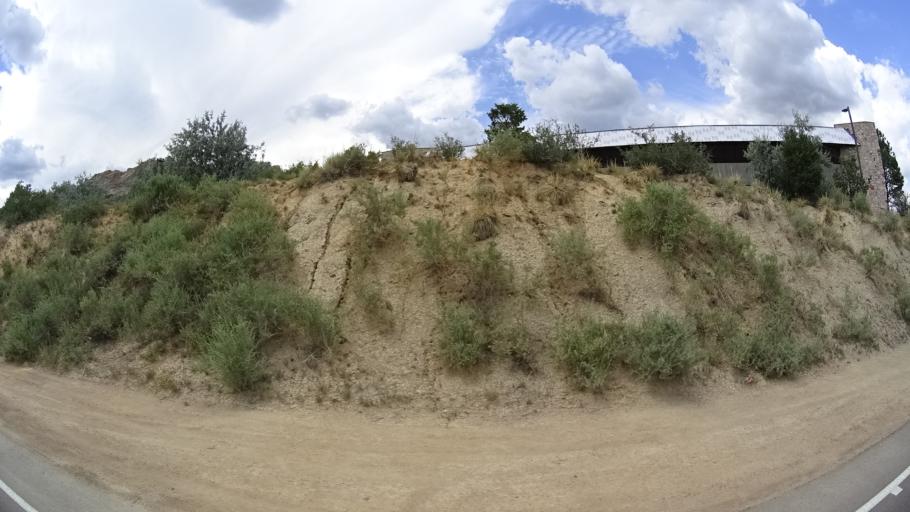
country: US
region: Colorado
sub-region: El Paso County
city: Manitou Springs
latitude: 38.8953
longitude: -104.8751
